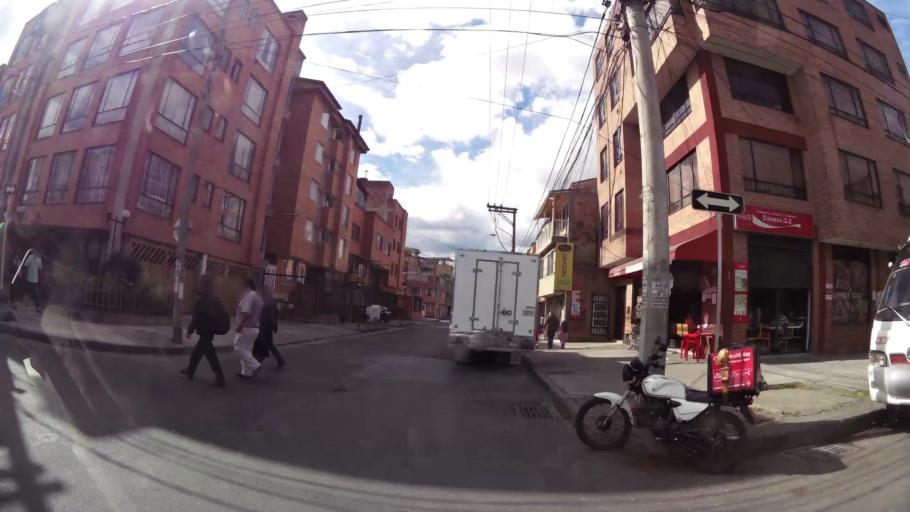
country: CO
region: Bogota D.C.
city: Bogota
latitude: 4.6136
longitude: -74.1324
